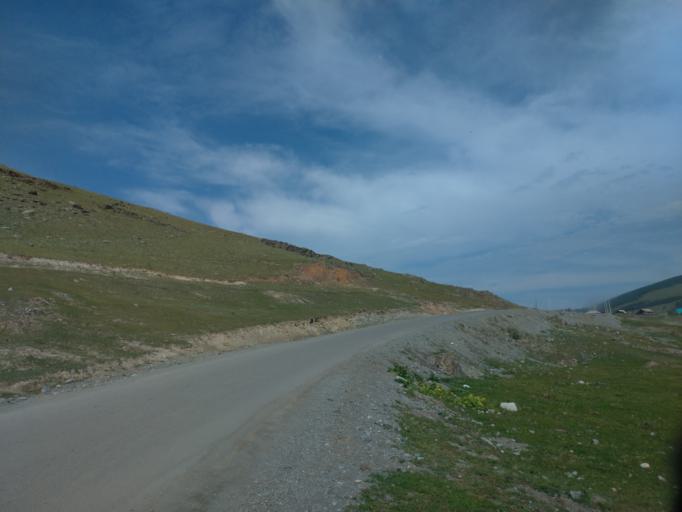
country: RU
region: Altay
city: Ust'-Ulagan
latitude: 50.6336
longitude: 87.9539
